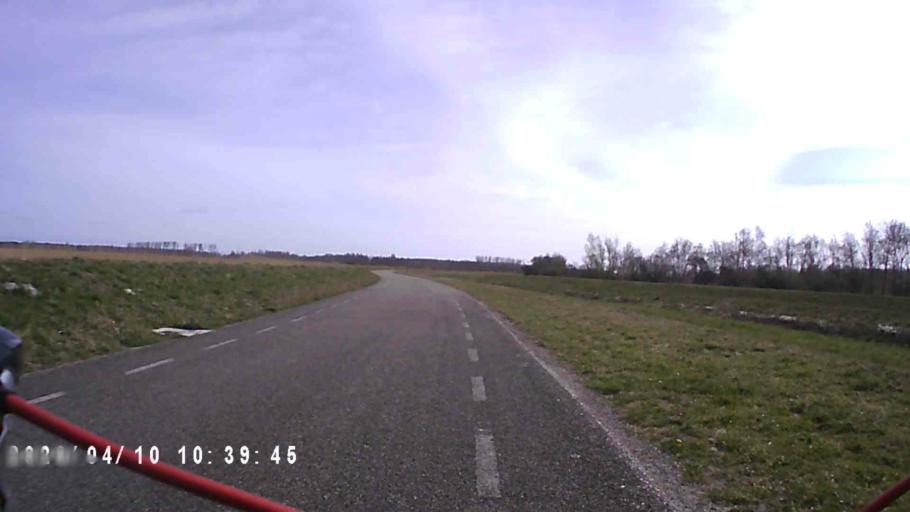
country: NL
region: Friesland
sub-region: Gemeente Dongeradeel
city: Anjum
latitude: 53.3851
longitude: 6.2298
